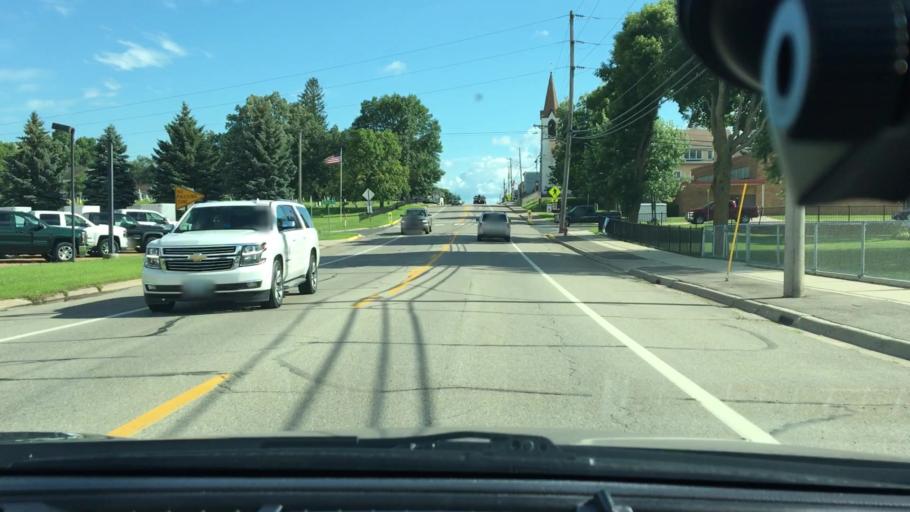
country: US
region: Minnesota
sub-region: Hennepin County
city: Saint Bonifacius
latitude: 44.9062
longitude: -93.7473
